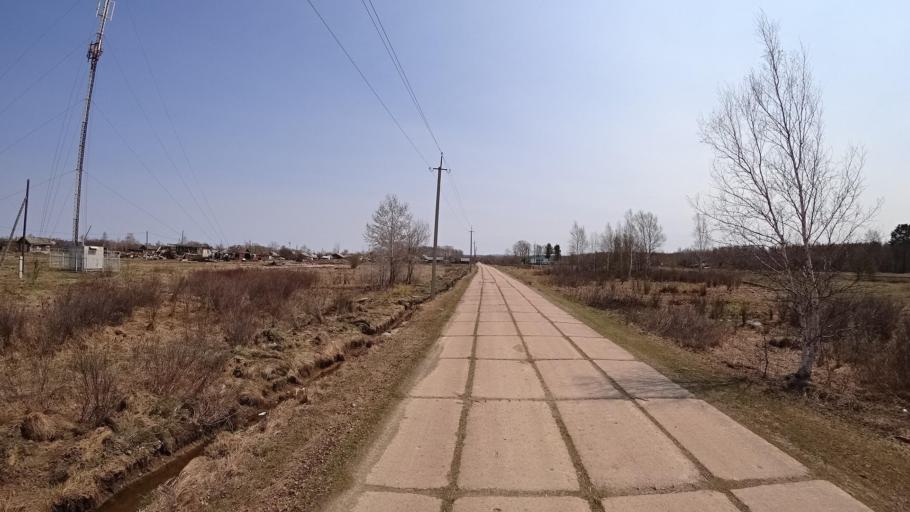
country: RU
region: Khabarovsk Krai
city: Selikhino
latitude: 50.3845
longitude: 137.3744
